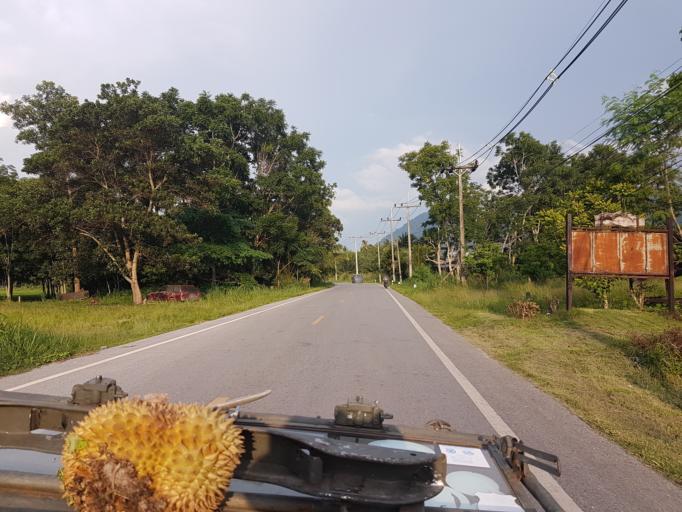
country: TH
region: Pattani
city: Khok Pho
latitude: 6.6753
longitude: 101.0965
